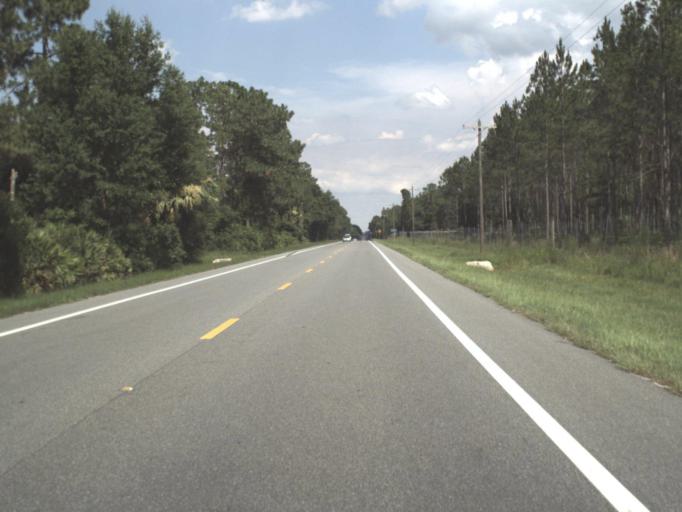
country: US
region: Florida
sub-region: Putnam County
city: Interlachen
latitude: 29.7144
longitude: -81.7999
